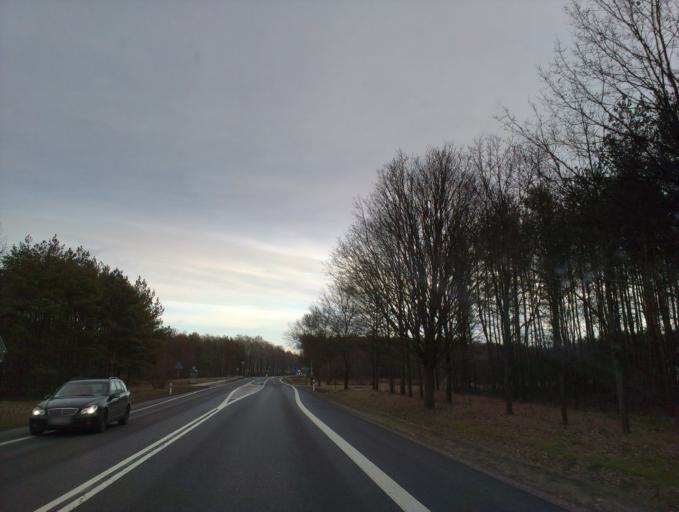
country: PL
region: Masovian Voivodeship
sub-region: Powiat sierpecki
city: Szczutowo
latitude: 52.8917
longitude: 19.5621
